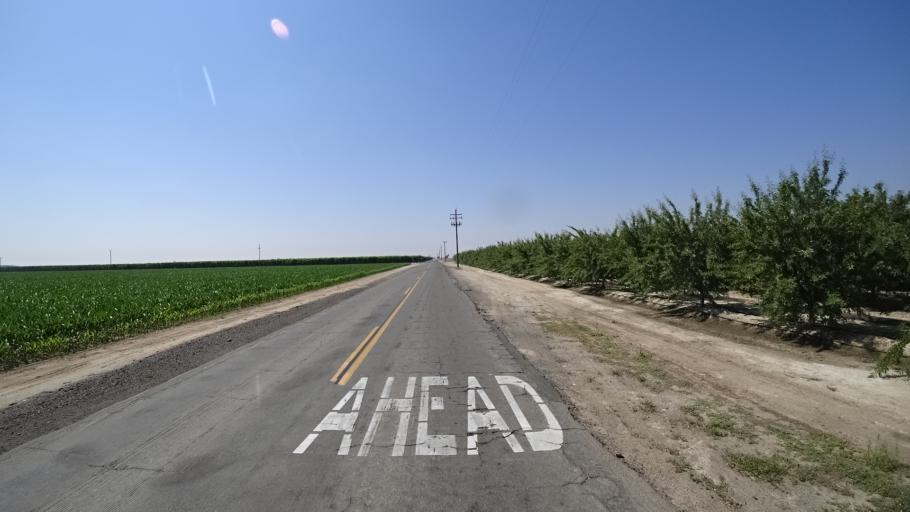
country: US
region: California
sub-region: Fresno County
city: Kingsburg
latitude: 36.4323
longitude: -119.5287
